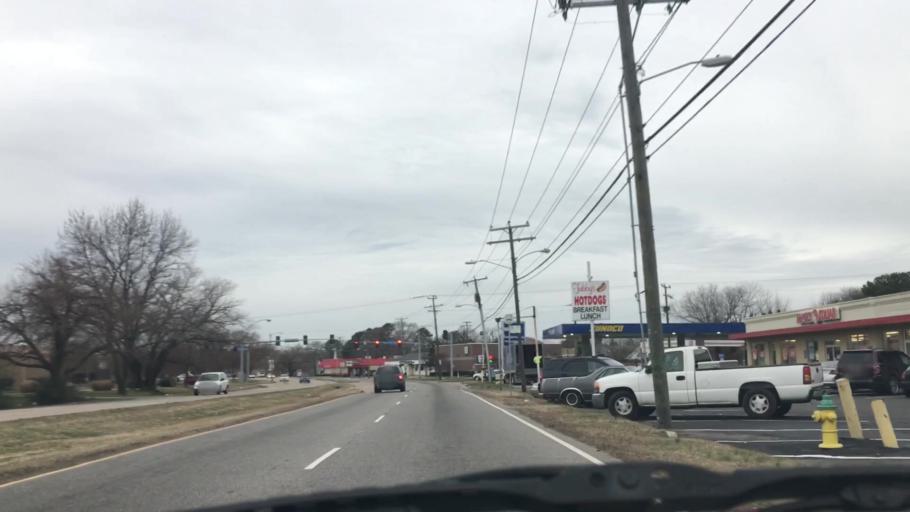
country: US
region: Virginia
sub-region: City of Norfolk
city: Norfolk
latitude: 36.8670
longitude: -76.2333
